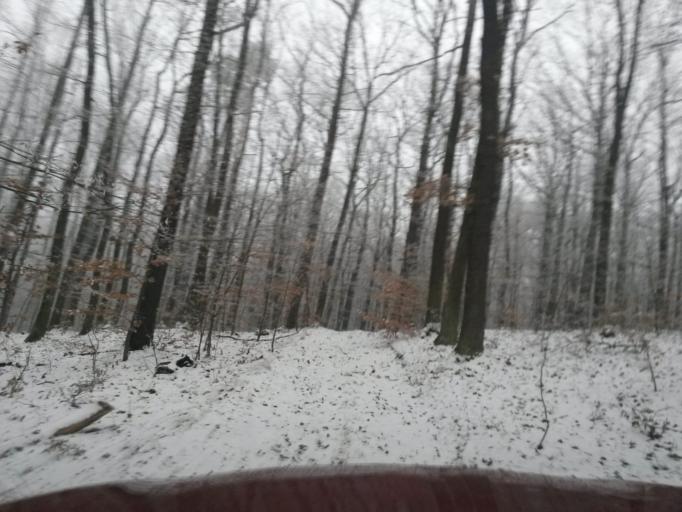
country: SK
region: Presovsky
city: Sabinov
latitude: 48.9755
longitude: 21.0914
